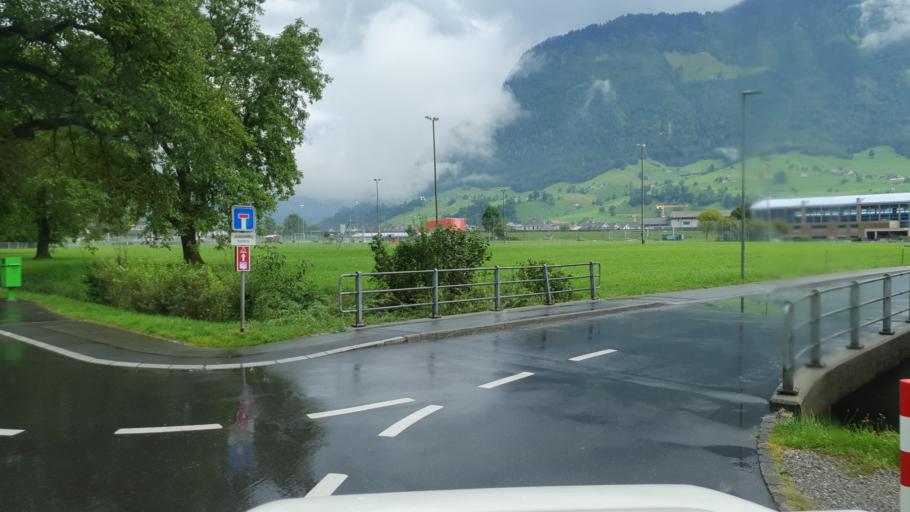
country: CH
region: Nidwalden
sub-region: Nidwalden
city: Stans
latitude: 46.9693
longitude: 8.3647
